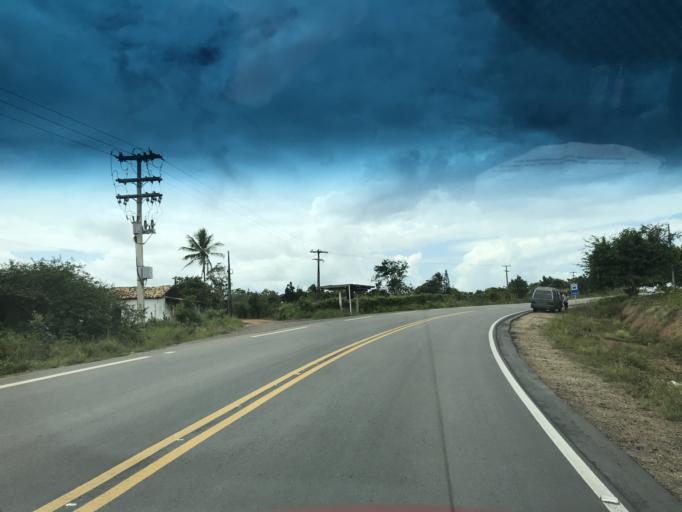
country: BR
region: Bahia
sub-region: Conceicao Do Almeida
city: Conceicao do Almeida
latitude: -12.6664
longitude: -39.2830
